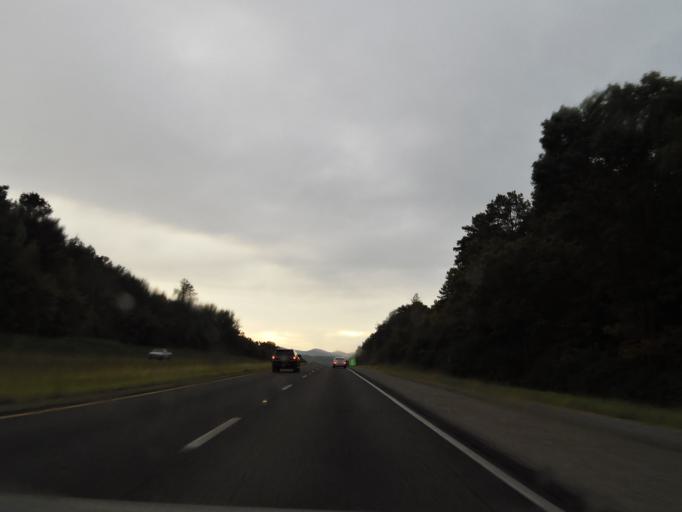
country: US
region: Alabama
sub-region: Saint Clair County
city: Springville
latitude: 33.7727
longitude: -86.4503
